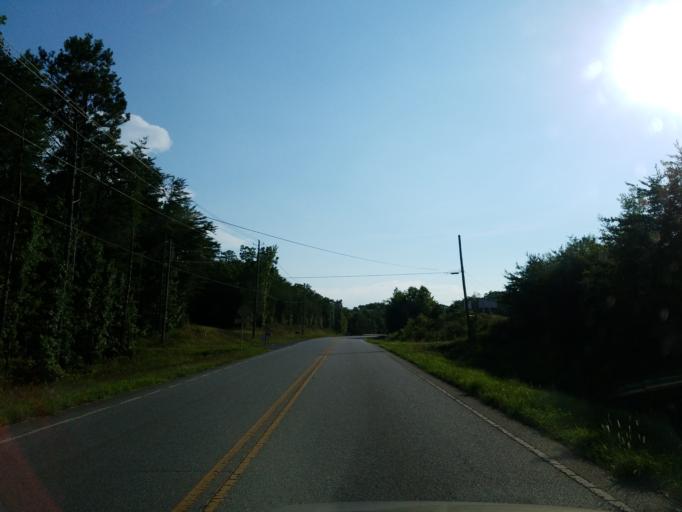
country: US
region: Georgia
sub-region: Bartow County
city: Rydal
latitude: 34.3393
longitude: -84.7266
